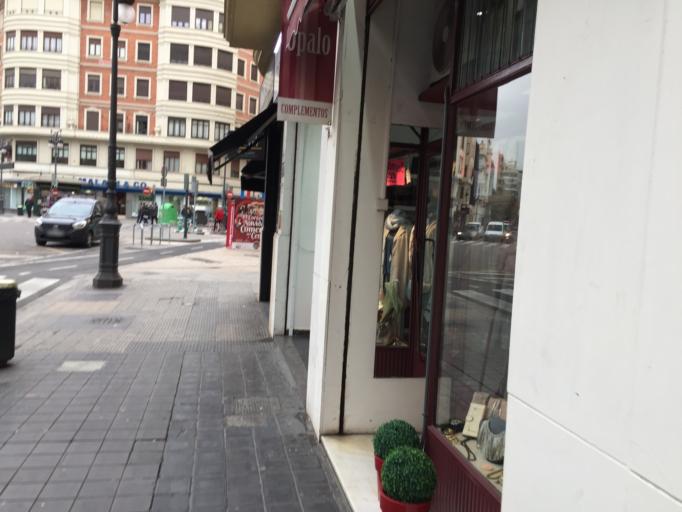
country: ES
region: Valencia
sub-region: Provincia de Valencia
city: Valencia
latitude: 39.4707
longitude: -0.3834
